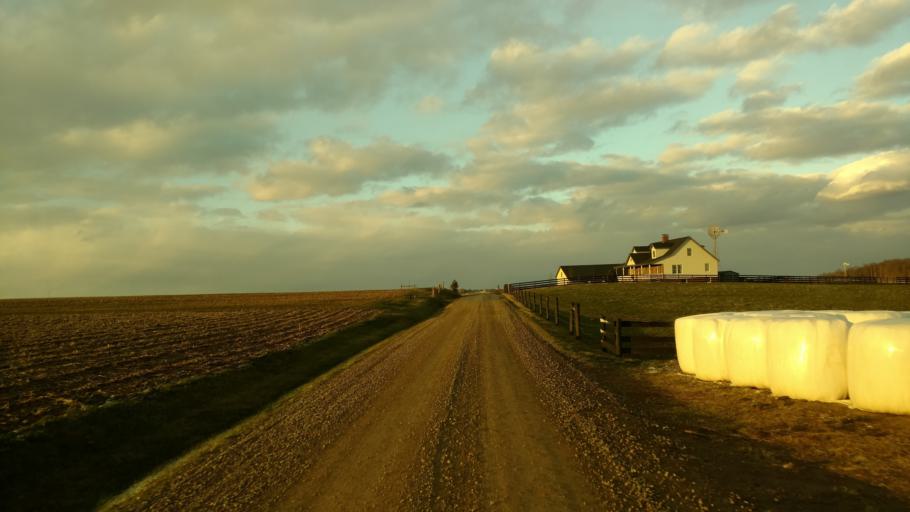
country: US
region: Ohio
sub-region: Tuscarawas County
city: Sugarcreek
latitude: 40.5108
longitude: -81.7699
